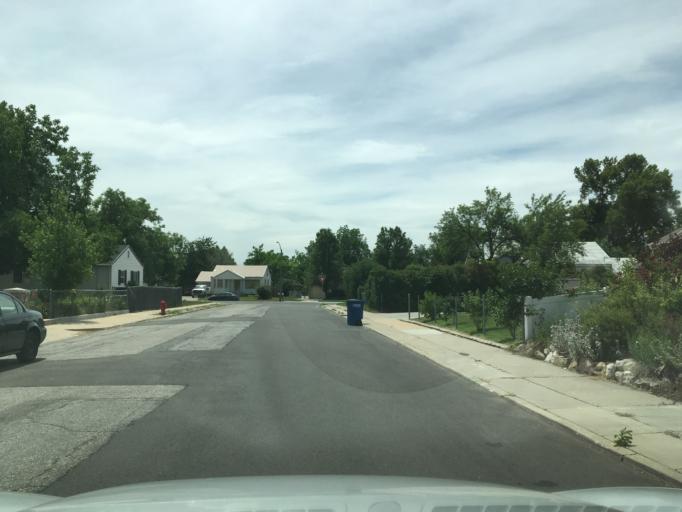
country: US
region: Utah
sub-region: Davis County
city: Layton
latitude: 41.0617
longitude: -111.9536
